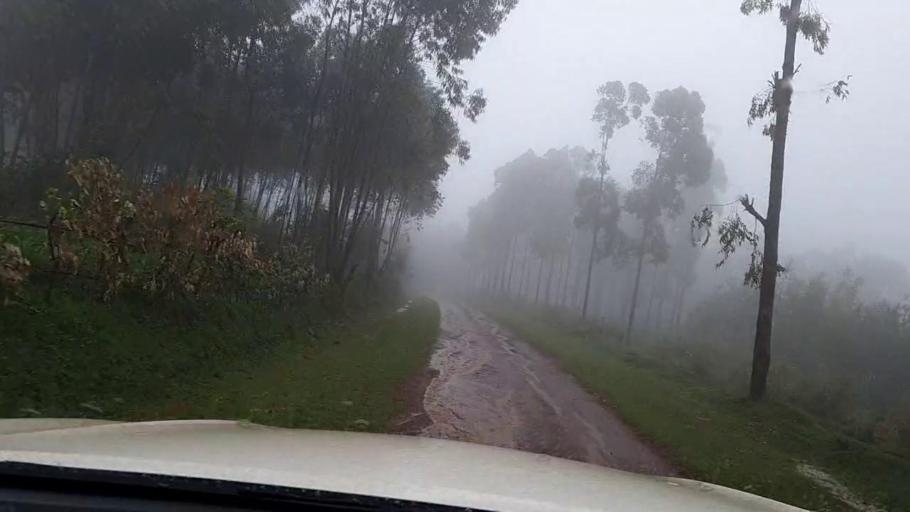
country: RW
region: Northern Province
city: Byumba
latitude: -1.7397
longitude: 30.0093
